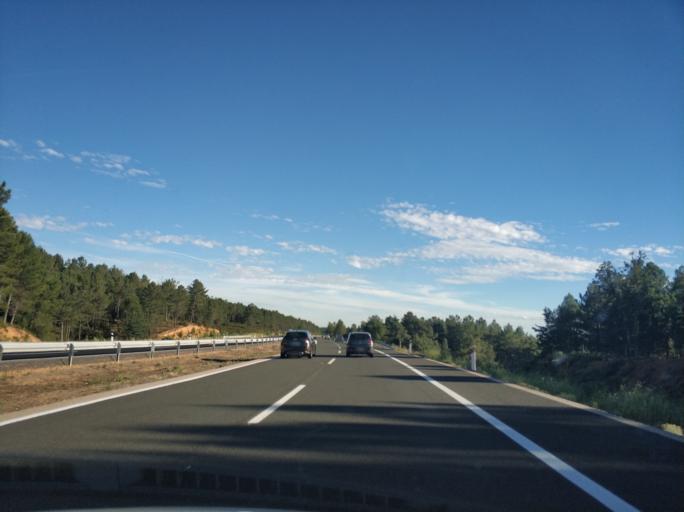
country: ES
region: Castille and Leon
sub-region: Provincia de Leon
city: Cimanes del Tejar
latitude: 42.6699
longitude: -5.7512
